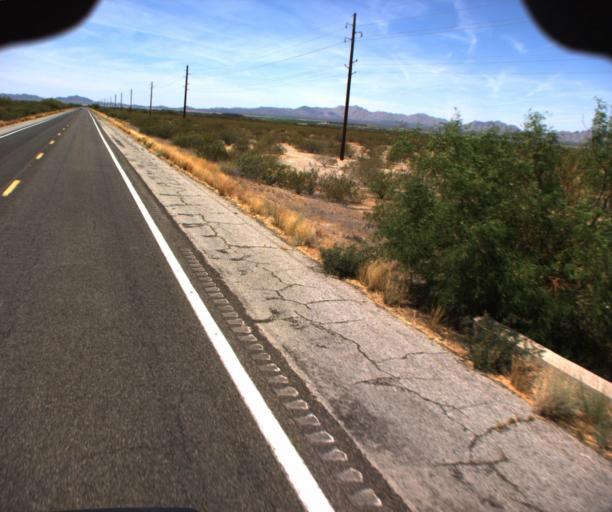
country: US
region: Arizona
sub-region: La Paz County
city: Salome
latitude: 33.8349
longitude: -113.4952
